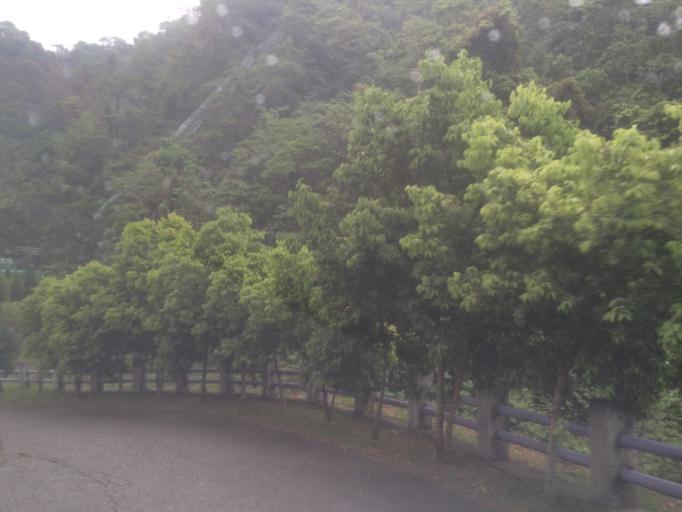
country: TW
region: Taiwan
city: Fengyuan
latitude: 24.1671
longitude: 120.8292
